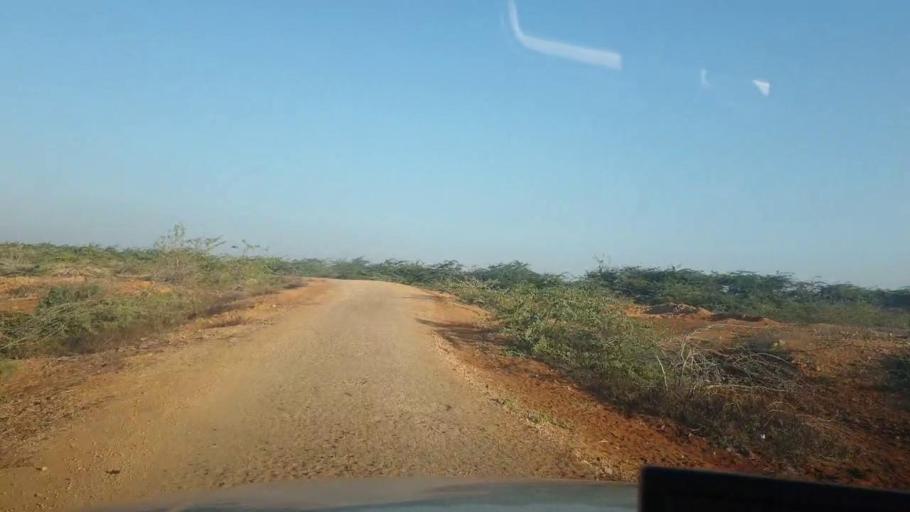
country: PK
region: Sindh
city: Thatta
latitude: 24.7060
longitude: 67.8486
